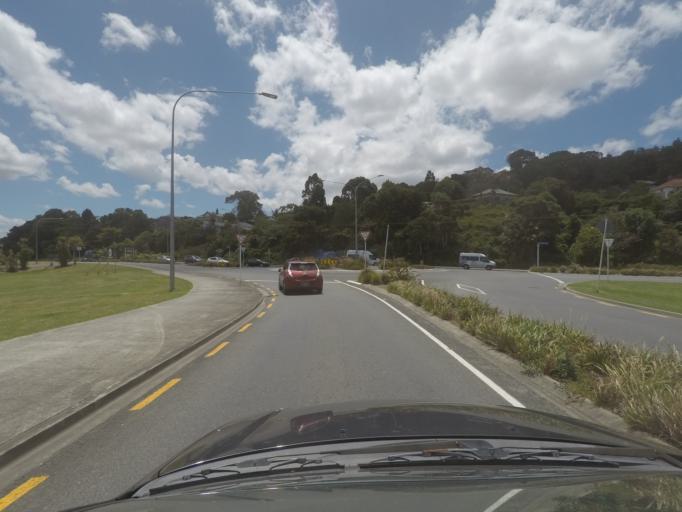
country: NZ
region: Northland
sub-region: Whangarei
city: Whangarei
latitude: -35.7314
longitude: 174.3426
